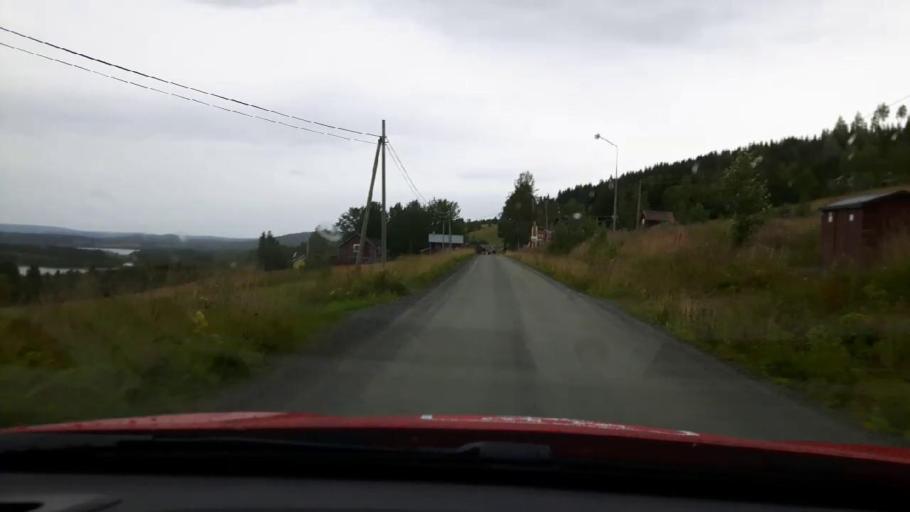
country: SE
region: Jaemtland
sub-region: Are Kommun
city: Are
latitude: 63.4596
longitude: 12.8200
